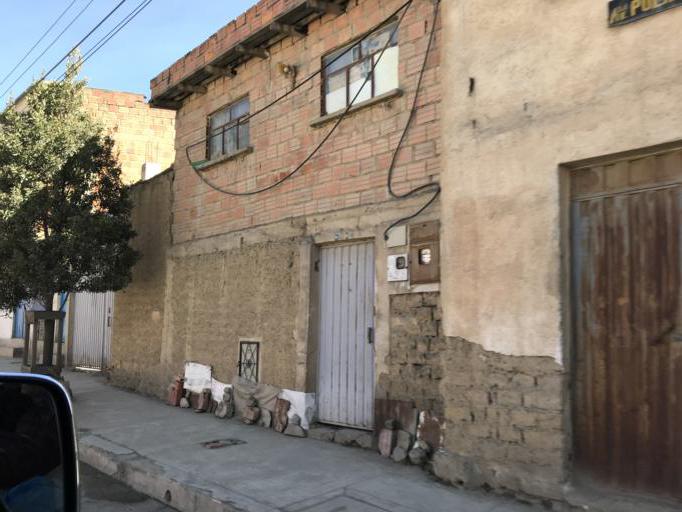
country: BO
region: La Paz
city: La Paz
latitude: -16.4867
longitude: -68.1786
